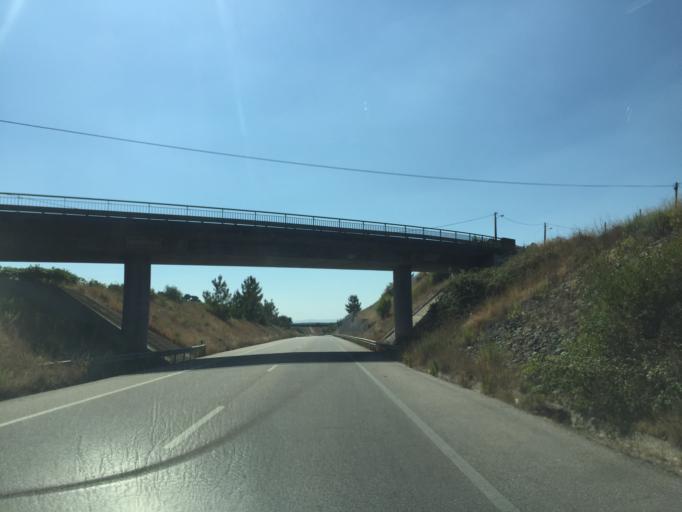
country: PT
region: Lisbon
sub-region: Azambuja
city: Aveiras de Cima
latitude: 39.1535
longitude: -8.8802
